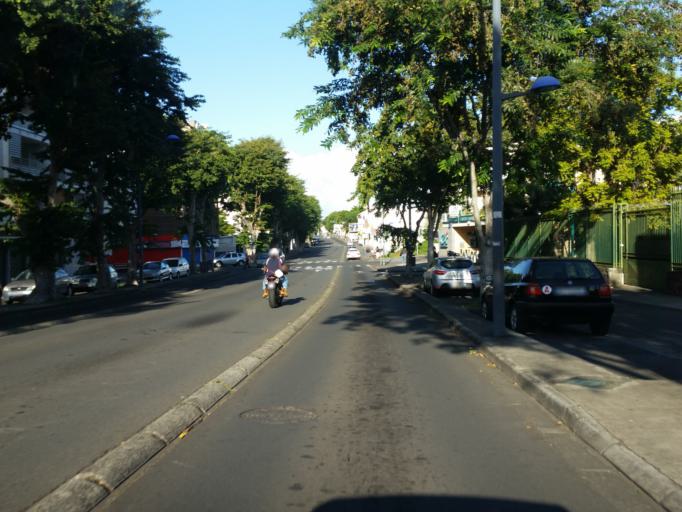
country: RE
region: Reunion
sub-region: Reunion
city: Saint-Denis
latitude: -20.8917
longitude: 55.4813
